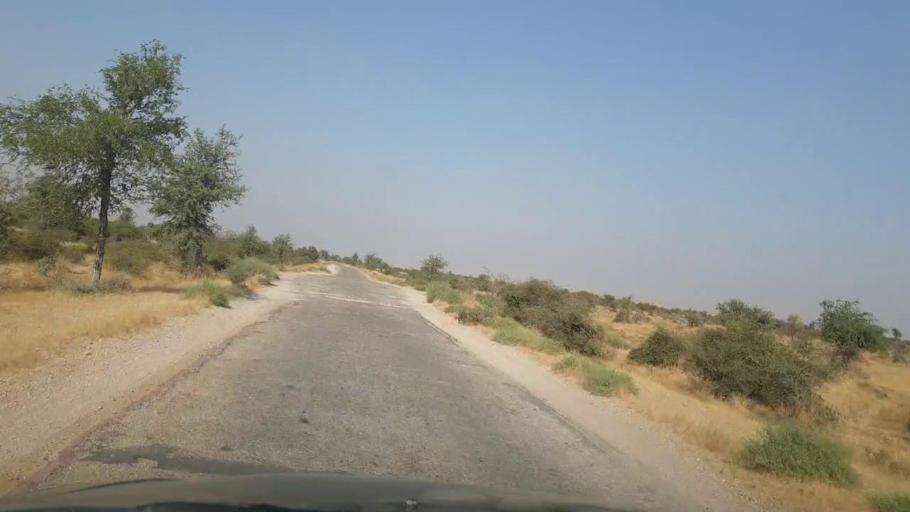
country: PK
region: Sindh
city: Jamshoro
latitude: 25.4822
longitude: 67.8234
